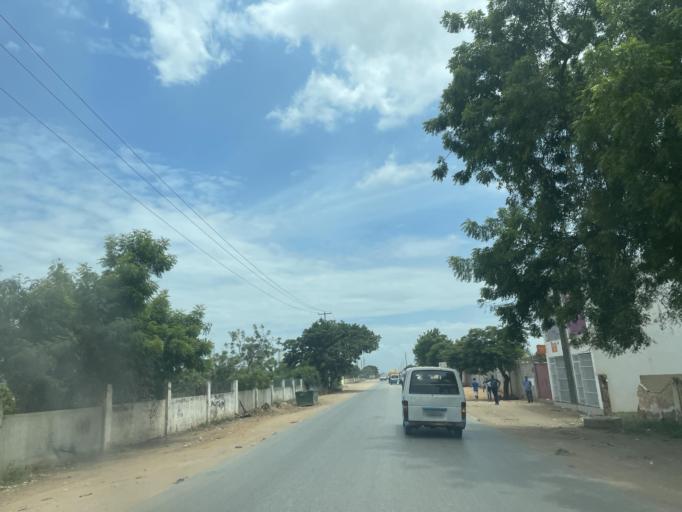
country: AO
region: Luanda
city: Luanda
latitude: -8.9330
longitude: 13.3815
